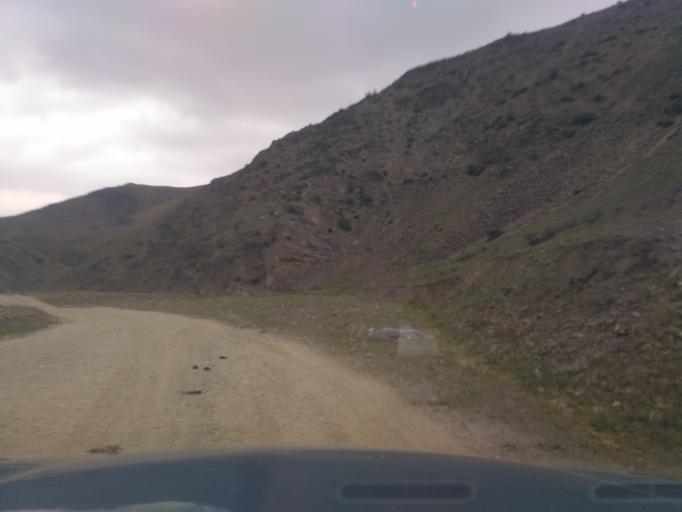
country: UZ
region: Jizzax
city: Zomin
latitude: 39.8501
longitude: 68.3965
